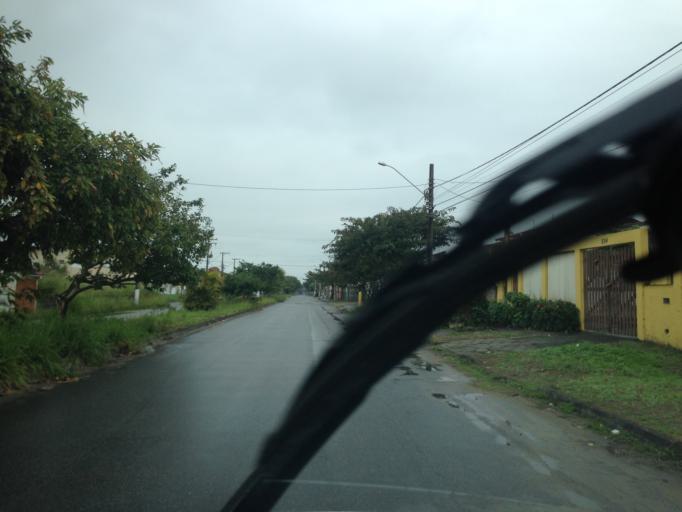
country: BR
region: Sao Paulo
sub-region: Itanhaem
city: Itanhaem
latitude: -24.2235
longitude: -46.8635
